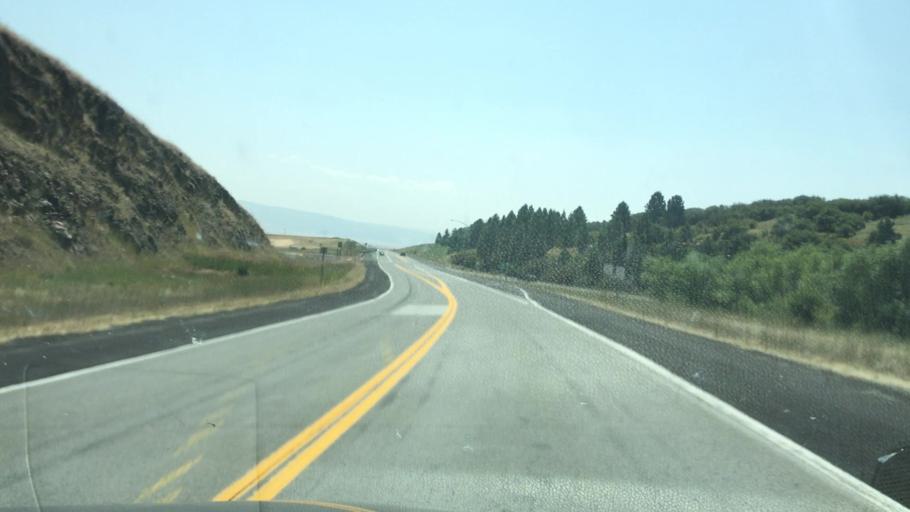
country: US
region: Idaho
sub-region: Lewis County
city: Nezperce
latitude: 46.0469
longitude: -116.3448
